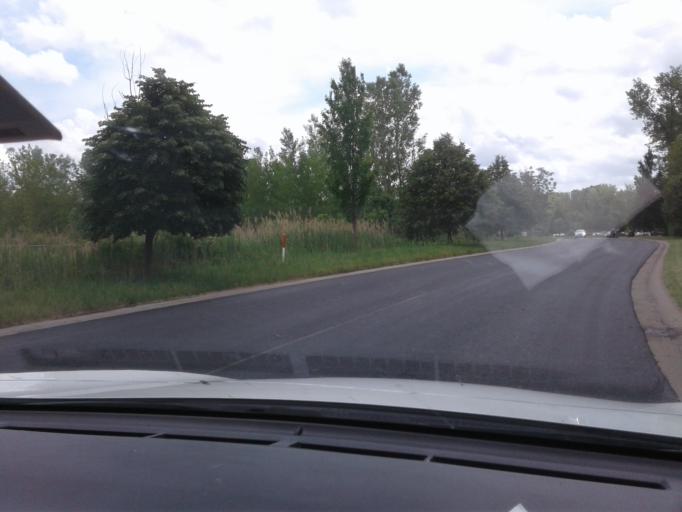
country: US
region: New York
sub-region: Onondaga County
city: East Syracuse
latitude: 43.0881
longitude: -76.0751
